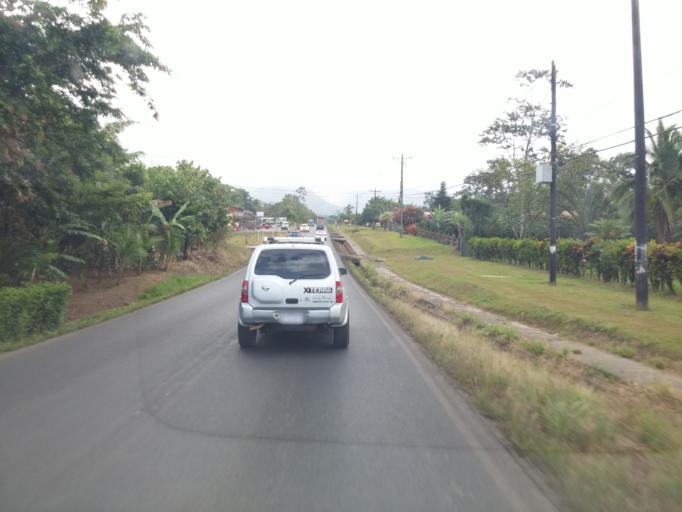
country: CR
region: Alajuela
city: Pital
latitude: 10.3862
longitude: -84.3396
